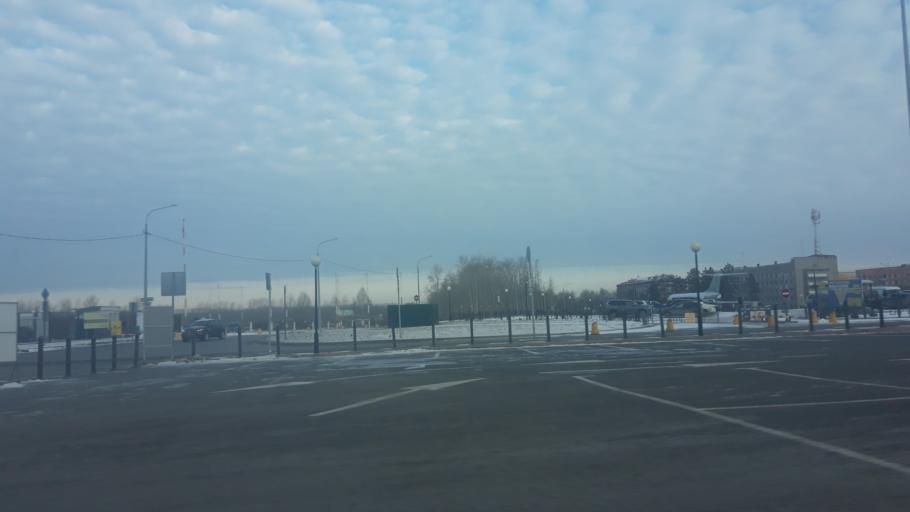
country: RU
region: Tjumen
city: Moskovskiy
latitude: 57.1824
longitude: 65.3485
